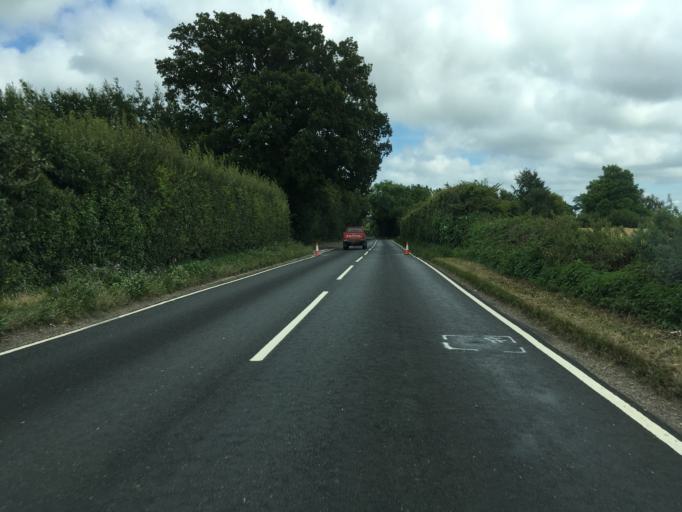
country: GB
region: England
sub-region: Kent
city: Cranbrook
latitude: 51.1116
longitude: 0.4838
